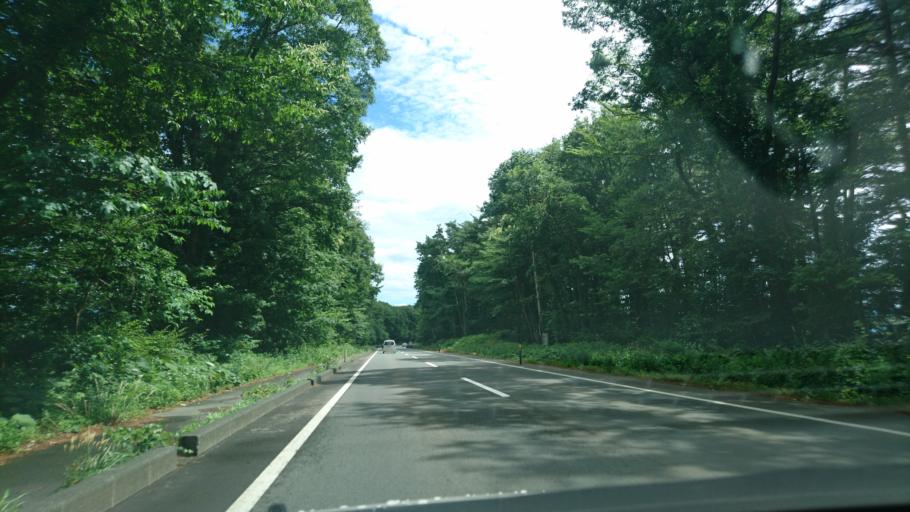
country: JP
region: Iwate
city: Morioka-shi
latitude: 39.7872
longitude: 141.1240
